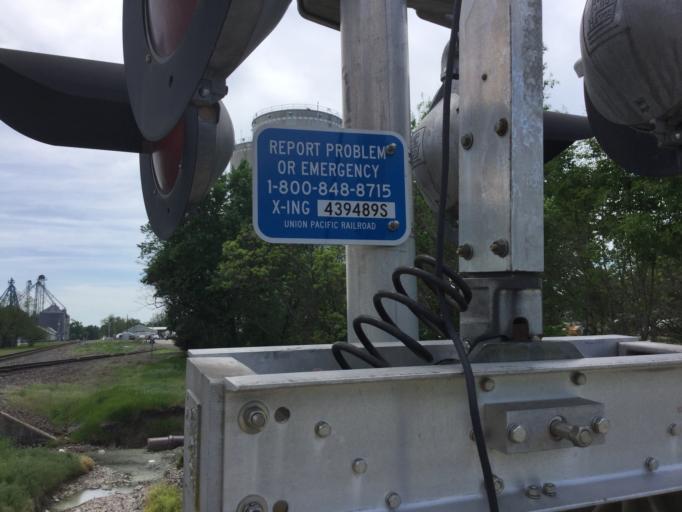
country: US
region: Kansas
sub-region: Coffey County
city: Burlington
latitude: 38.0844
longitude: -95.6309
